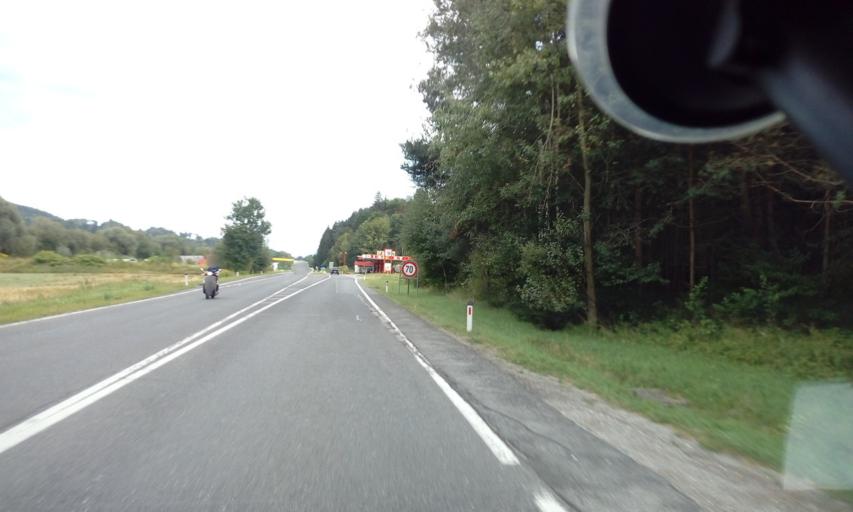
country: AT
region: Carinthia
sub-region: Villach Stadt
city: Villach
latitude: 46.6375
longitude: 13.8122
